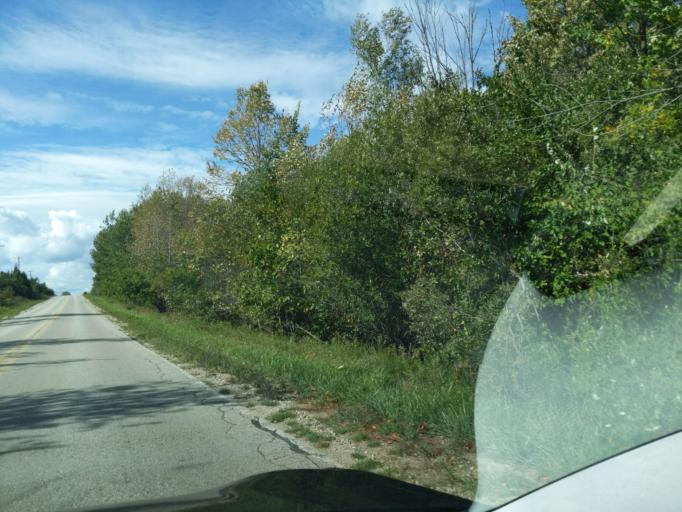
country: US
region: Michigan
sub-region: Antrim County
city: Bellaire
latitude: 45.0347
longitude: -85.3424
